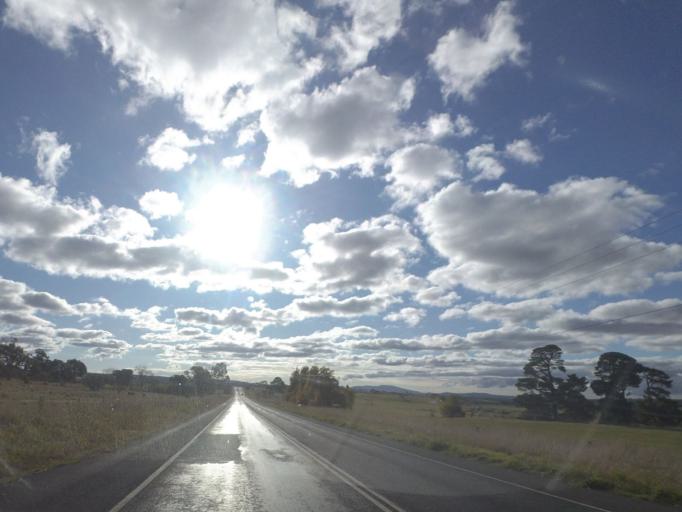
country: AU
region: Victoria
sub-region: Mount Alexander
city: Castlemaine
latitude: -37.1831
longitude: 144.3640
